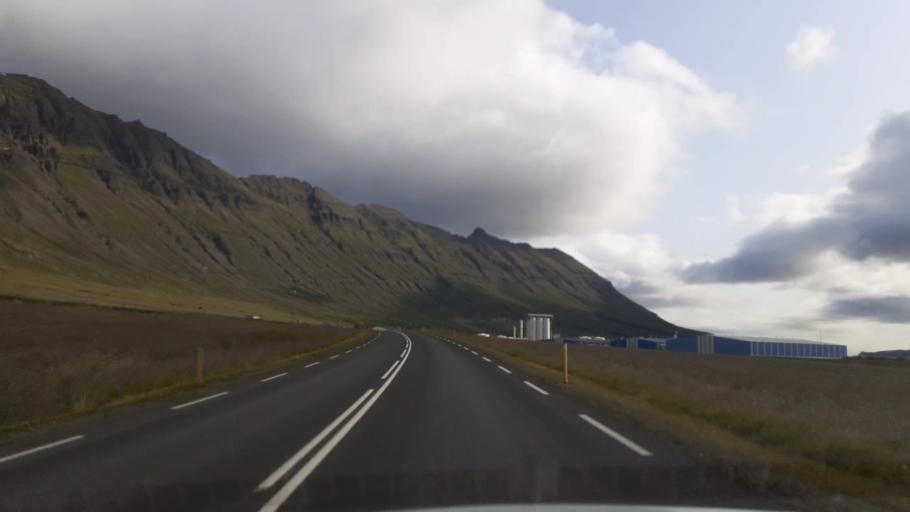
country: IS
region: East
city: Neskaupstadur
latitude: 65.1343
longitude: -13.7523
